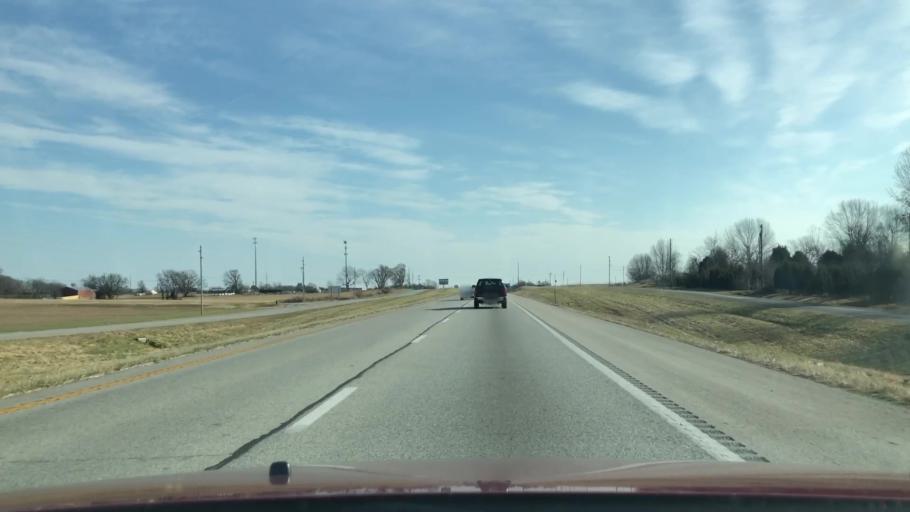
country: US
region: Missouri
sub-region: Christian County
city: Ozark
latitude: 37.1207
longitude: -93.2064
